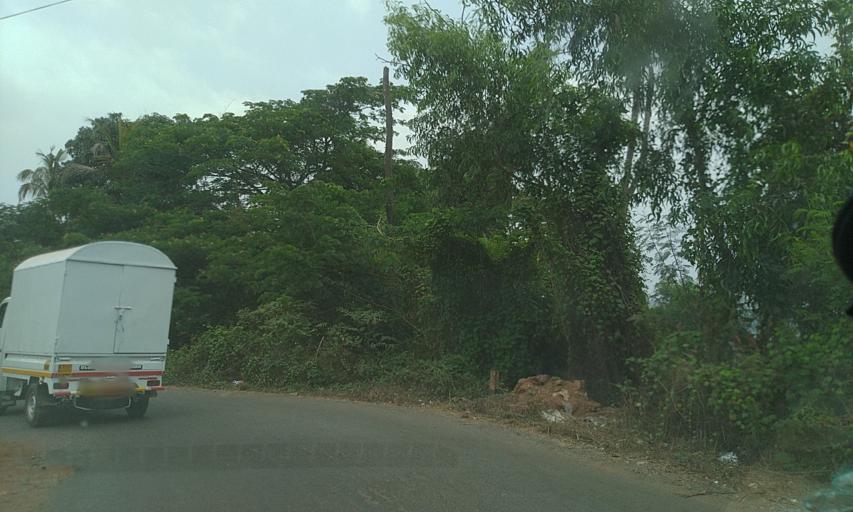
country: IN
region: Goa
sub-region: North Goa
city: Jua
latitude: 15.4859
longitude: 73.9251
